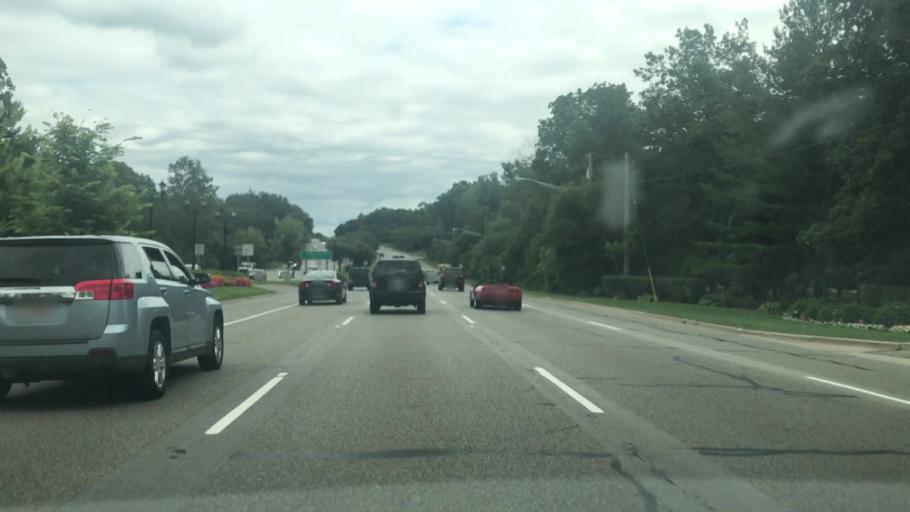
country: US
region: Michigan
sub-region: Oakland County
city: Bloomfield Hills
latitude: 42.5952
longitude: -83.2565
